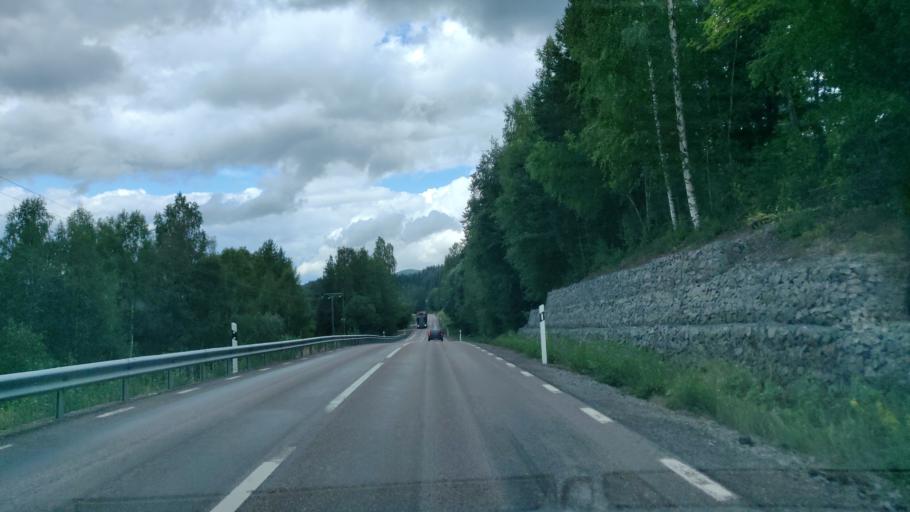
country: SE
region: Vaermland
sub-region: Torsby Kommun
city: Torsby
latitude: 60.5924
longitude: 13.0742
